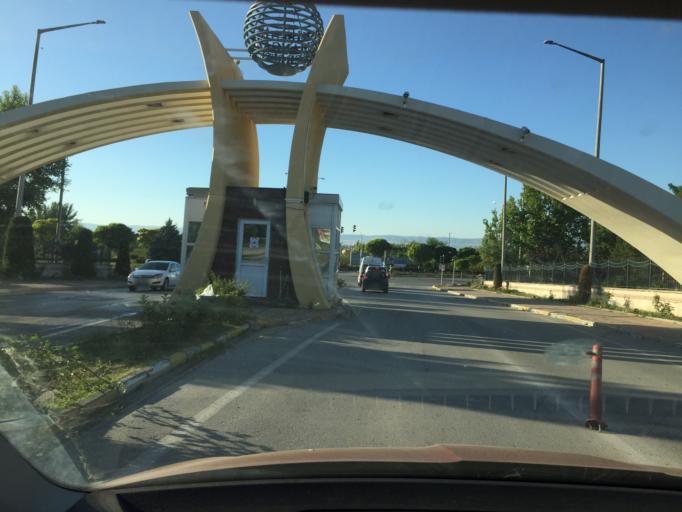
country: TR
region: Eskisehir
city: Eskisehir
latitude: 39.7540
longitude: 30.4882
